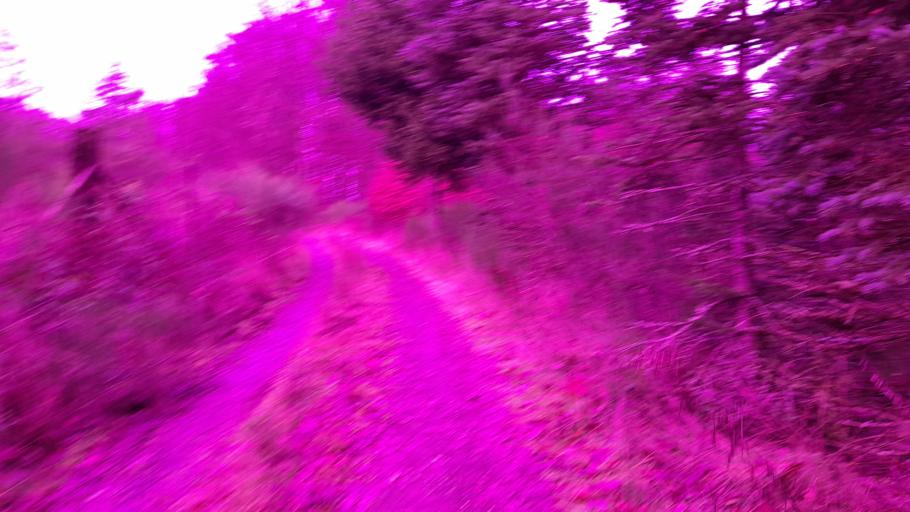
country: DE
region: Rheinland-Pfalz
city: Dasburg
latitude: 50.0702
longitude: 6.1182
